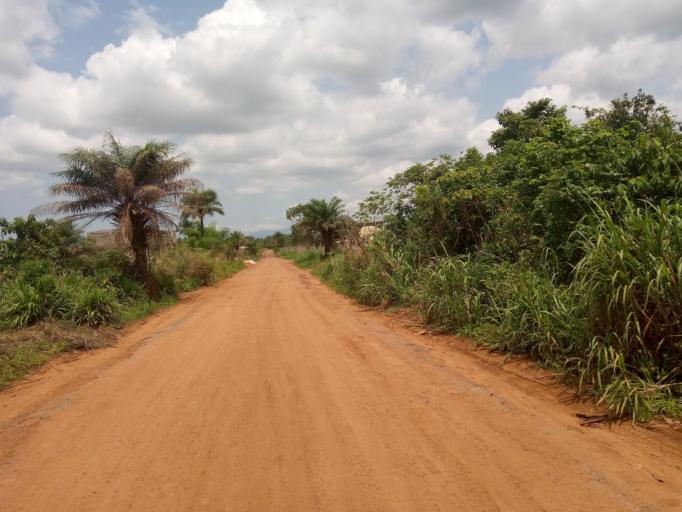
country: SL
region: Western Area
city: Waterloo
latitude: 8.3862
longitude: -12.9538
